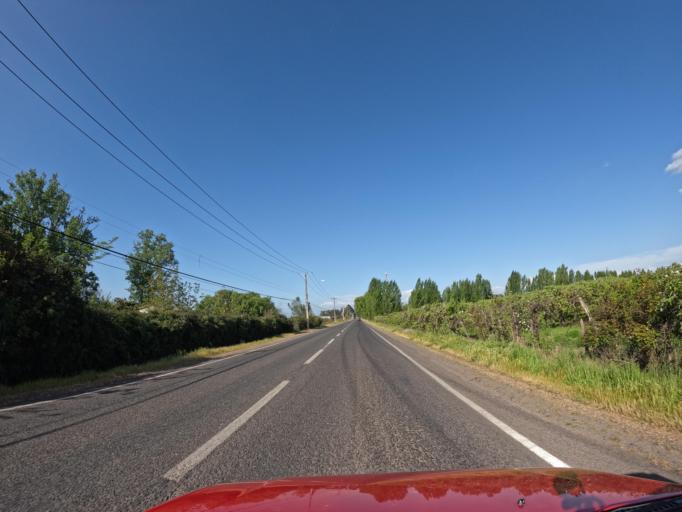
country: CL
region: Maule
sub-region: Provincia de Curico
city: Teno
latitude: -34.8692
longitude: -71.2159
